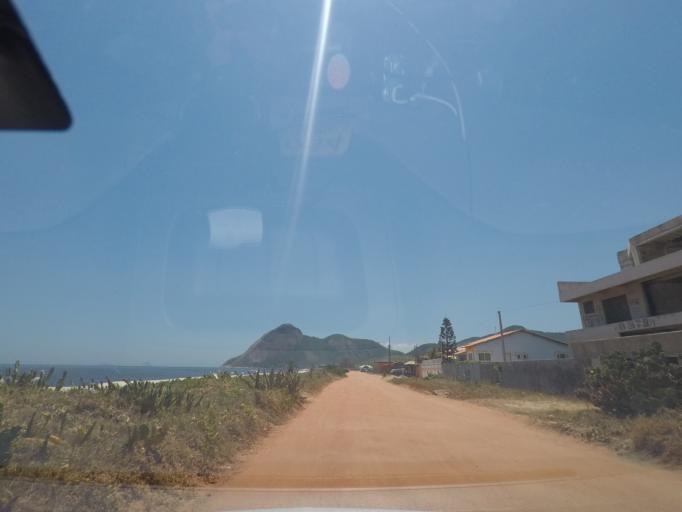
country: BR
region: Rio de Janeiro
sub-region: Niteroi
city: Niteroi
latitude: -22.9690
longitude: -42.9867
